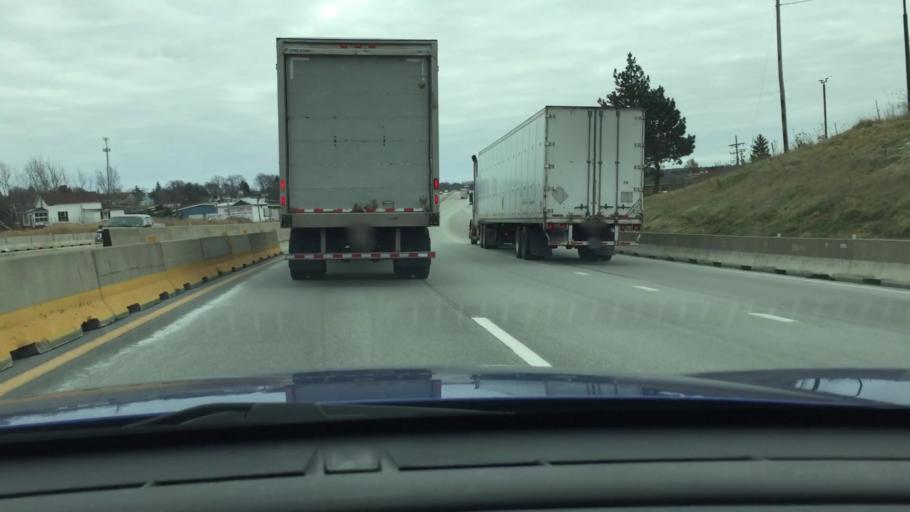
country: US
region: Pennsylvania
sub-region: Somerset County
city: Somerset
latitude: 40.0185
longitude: -79.0775
